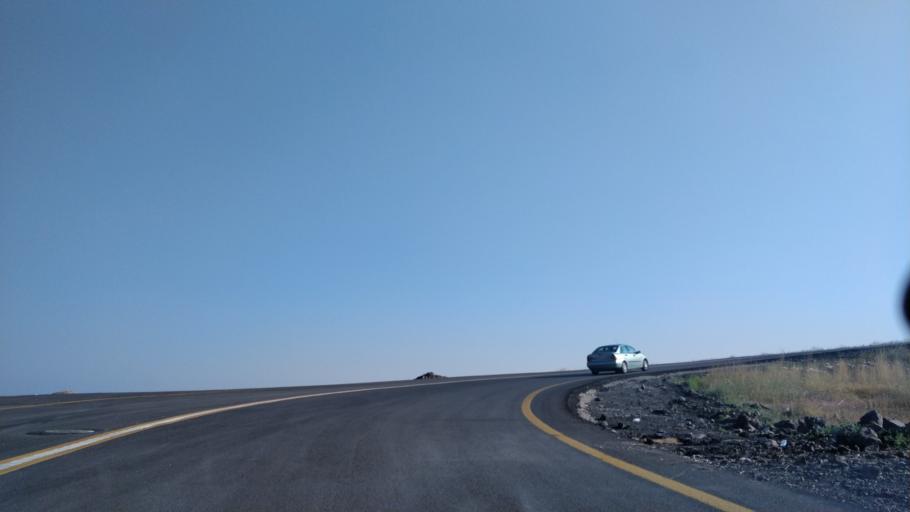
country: TR
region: Ankara
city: Etimesgut
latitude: 39.8464
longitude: 32.5454
